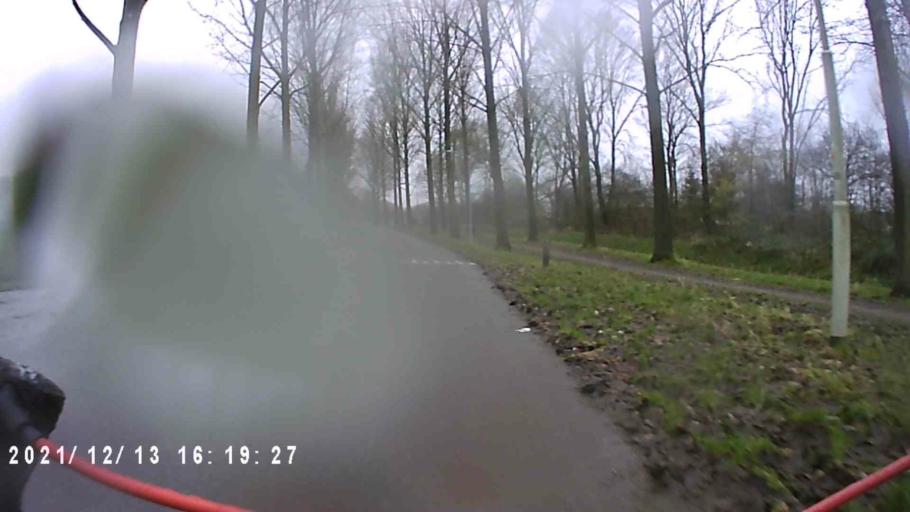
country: NL
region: Groningen
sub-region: Gemeente Delfzijl
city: Delfzijl
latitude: 53.3403
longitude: 6.8968
